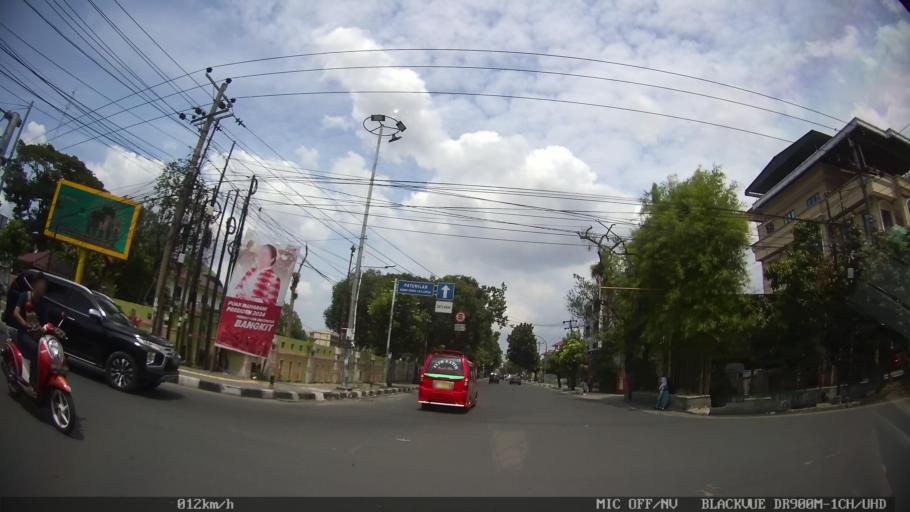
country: ID
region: North Sumatra
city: Medan
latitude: 3.5847
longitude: 98.6616
